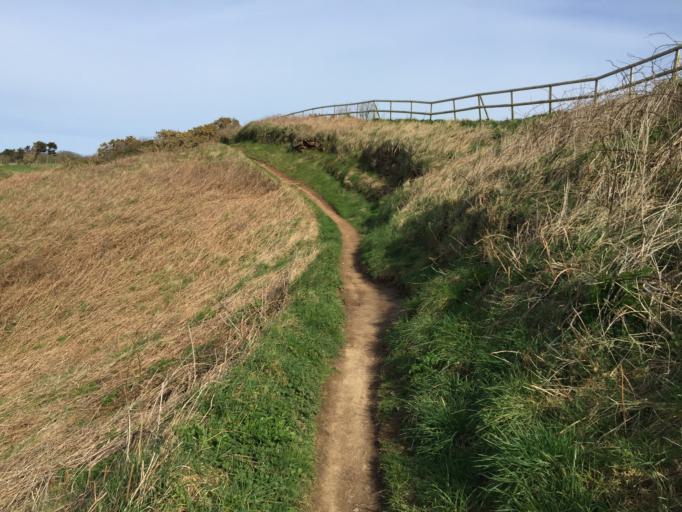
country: JE
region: St Helier
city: Saint Helier
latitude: 49.2487
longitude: -2.1748
